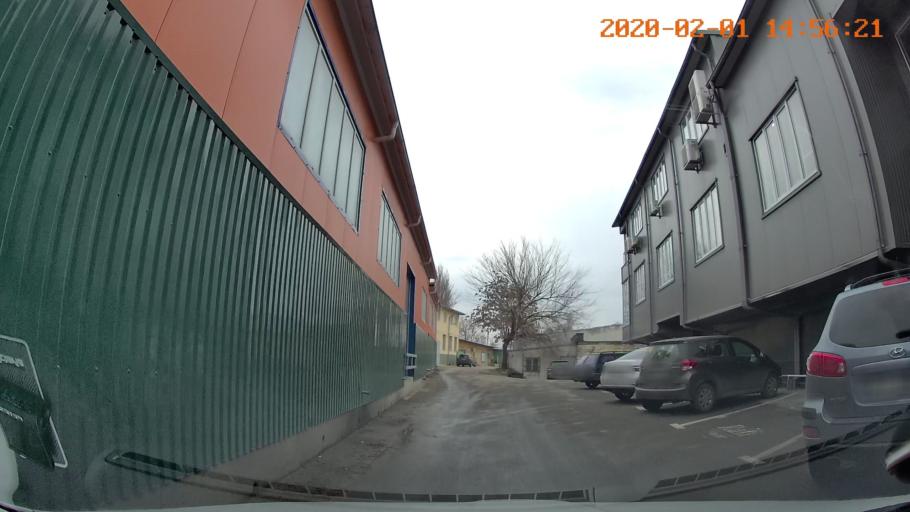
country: MD
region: Chisinau
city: Chisinau
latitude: 47.0125
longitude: 28.8789
